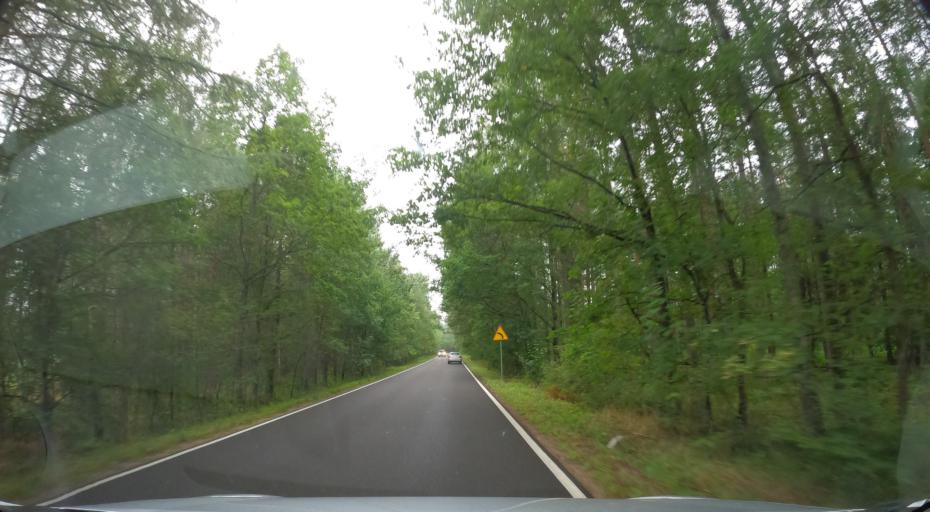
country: PL
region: Pomeranian Voivodeship
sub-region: Powiat wejherowski
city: Linia
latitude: 54.4918
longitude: 17.8419
